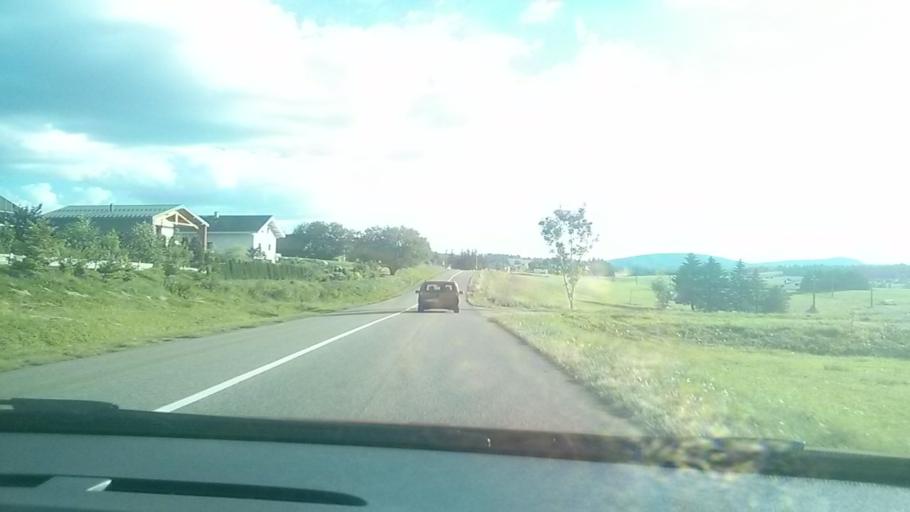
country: FR
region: Franche-Comte
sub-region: Departement du Jura
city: Les Rousses
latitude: 46.4959
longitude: 6.0966
